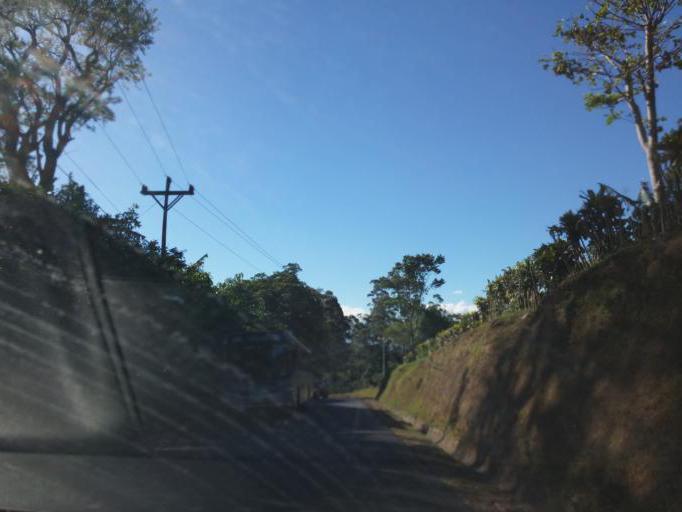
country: CR
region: Alajuela
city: Sabanilla
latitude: 10.0666
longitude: -84.2080
